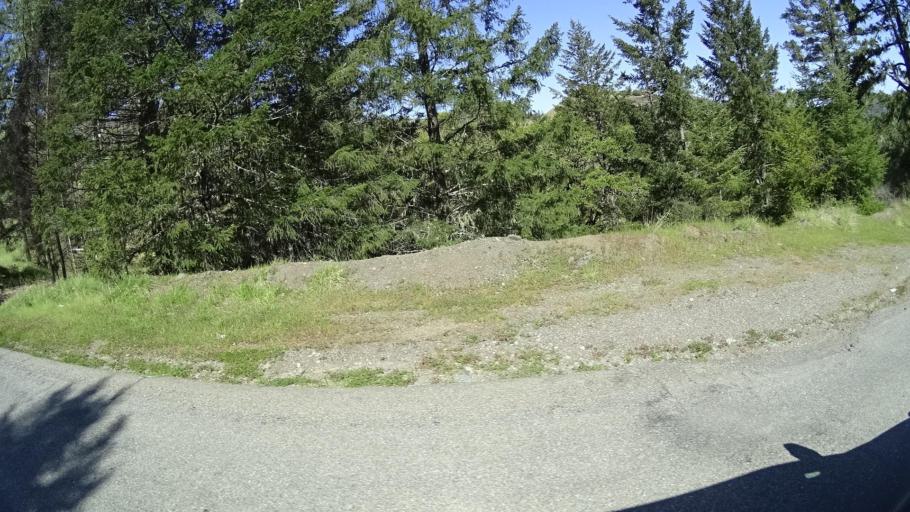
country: US
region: California
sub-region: Humboldt County
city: Redway
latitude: 40.0852
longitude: -123.6654
